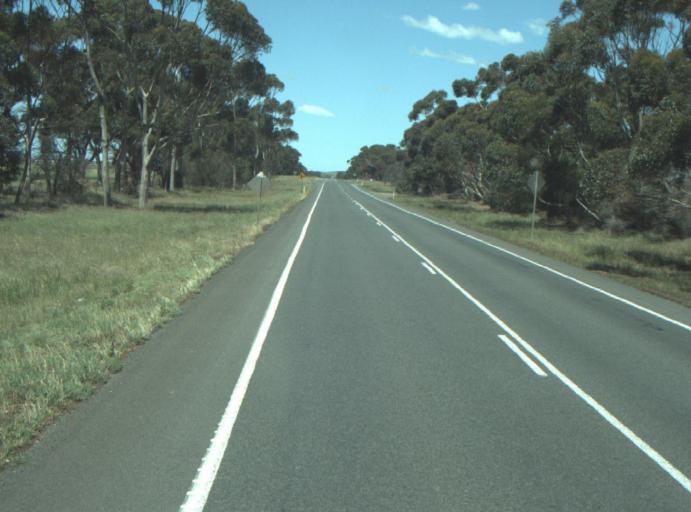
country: AU
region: Victoria
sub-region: Greater Geelong
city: Lara
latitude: -37.9567
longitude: 144.3519
